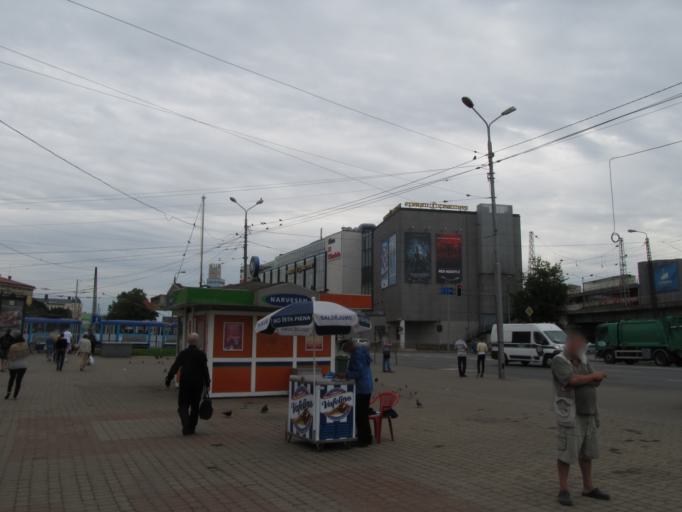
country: LV
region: Riga
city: Riga
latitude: 56.9457
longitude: 24.1138
